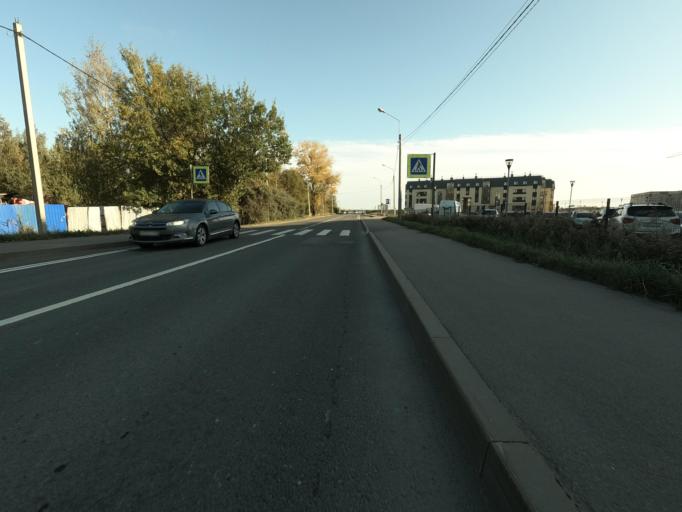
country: RU
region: St.-Petersburg
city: Pontonnyy
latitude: 59.7566
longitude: 30.6300
